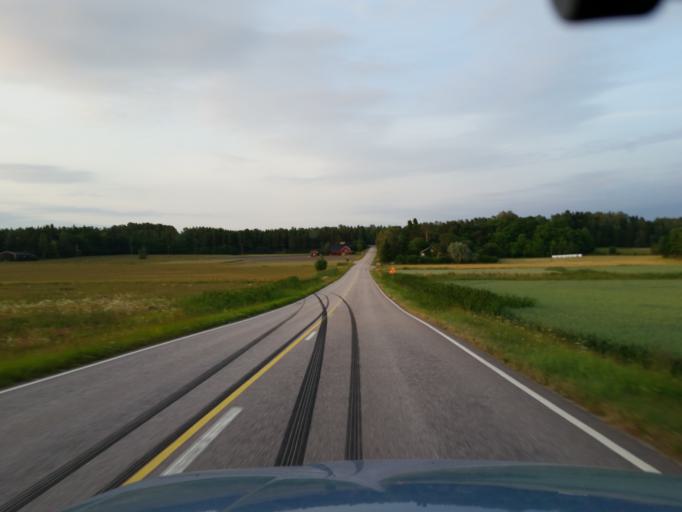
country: FI
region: Varsinais-Suomi
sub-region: Aboland-Turunmaa
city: Nagu
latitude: 60.1921
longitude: 22.0372
